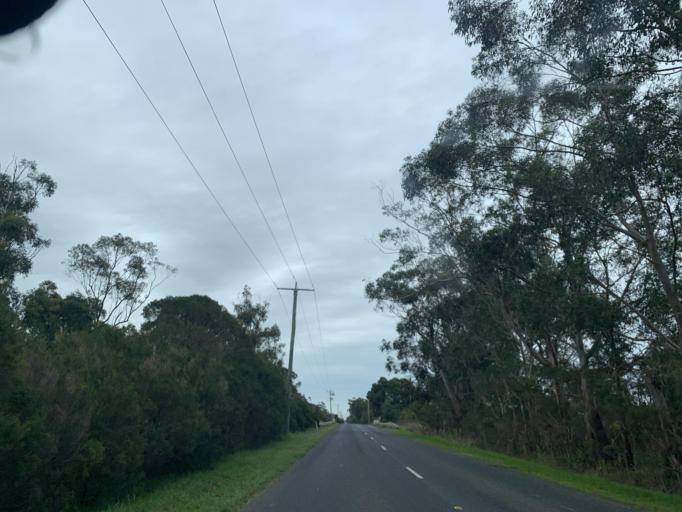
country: AU
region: Victoria
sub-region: Cardinia
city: Garfield
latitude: -38.0832
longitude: 145.5944
